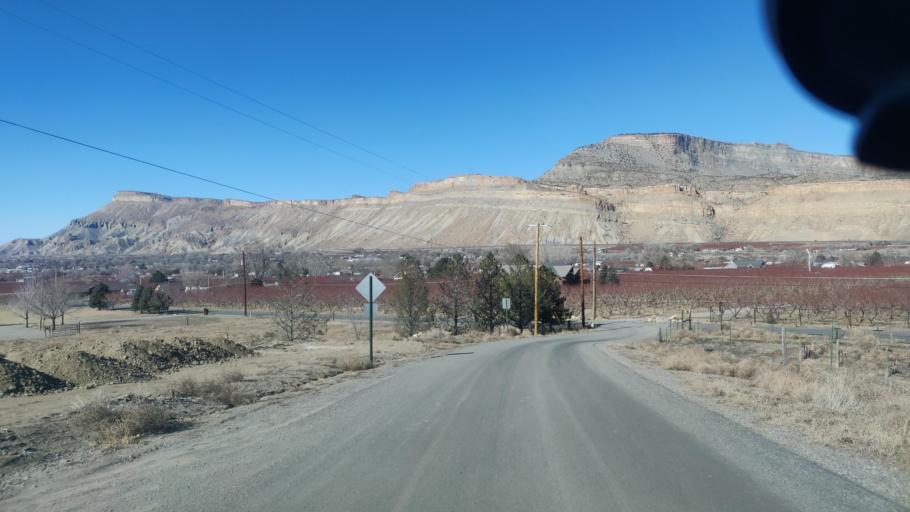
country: US
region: Colorado
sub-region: Mesa County
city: Palisade
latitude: 39.1013
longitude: -108.3314
